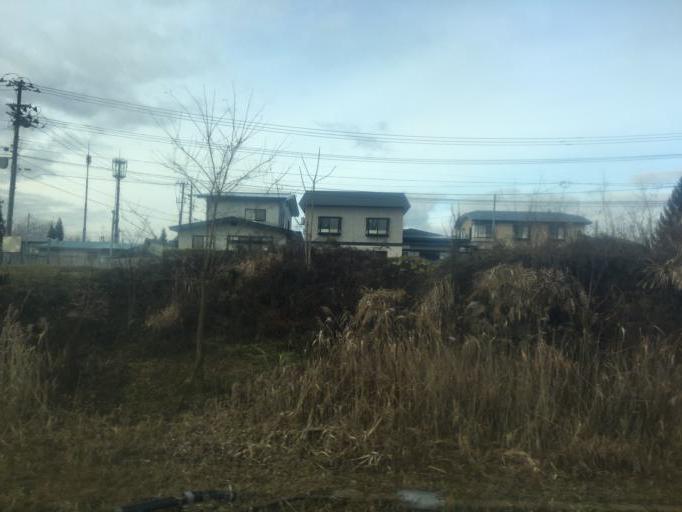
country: JP
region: Akita
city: Odate
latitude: 40.2992
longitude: 140.5670
